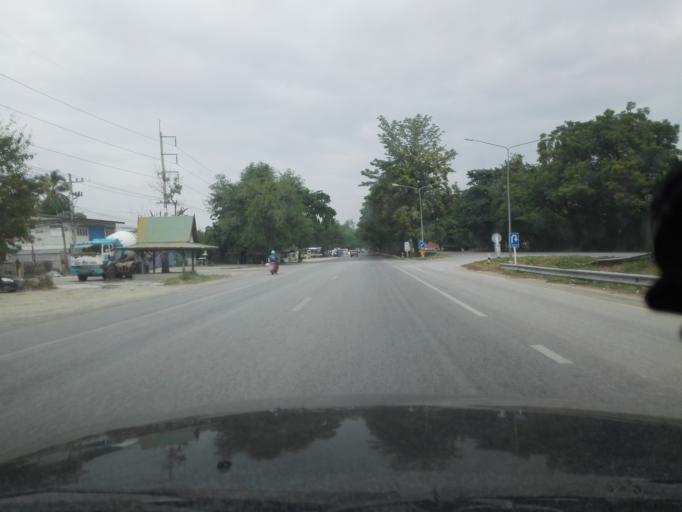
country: TH
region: Nakhon Sawan
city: Nakhon Sawan
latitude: 15.7310
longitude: 100.0332
